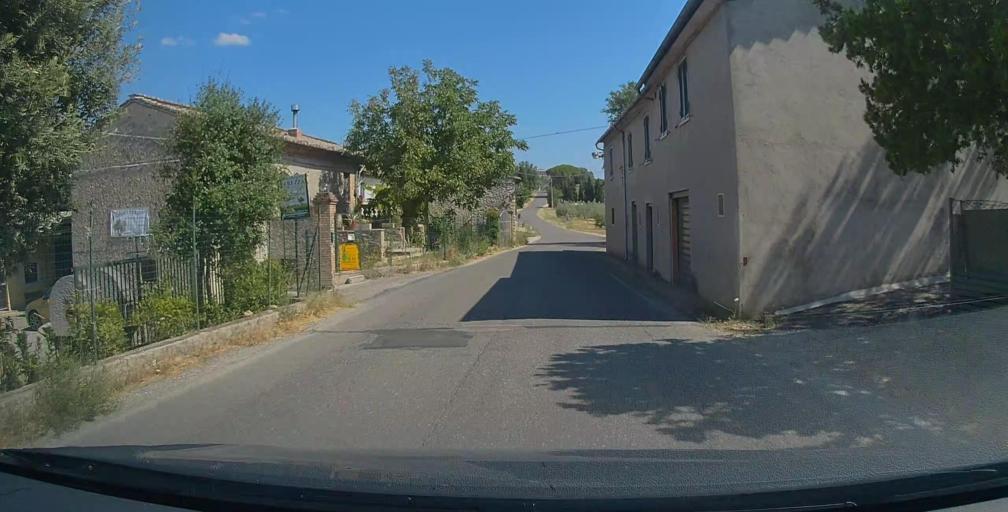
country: IT
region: Umbria
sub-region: Provincia di Terni
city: Calvi dell'Umbria
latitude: 42.4104
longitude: 12.5575
